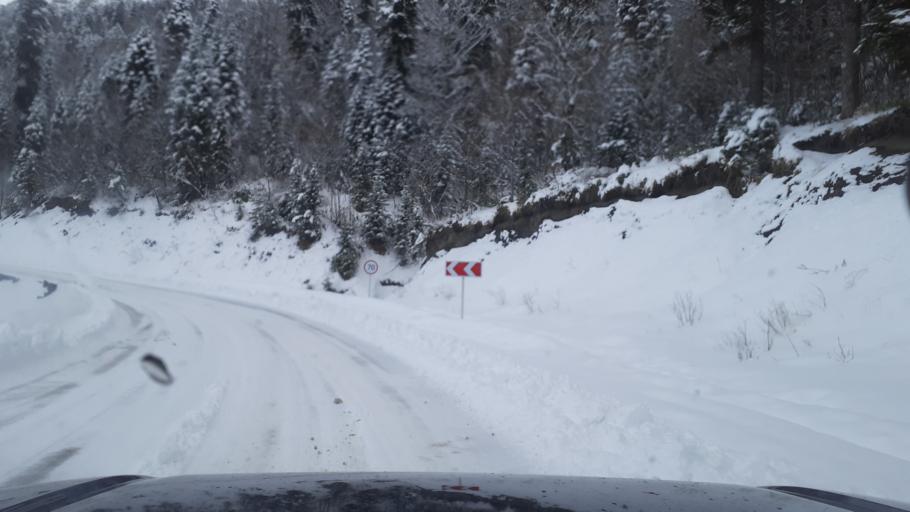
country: RU
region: Adygeya
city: Kamennomostskiy
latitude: 44.0109
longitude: 40.0070
